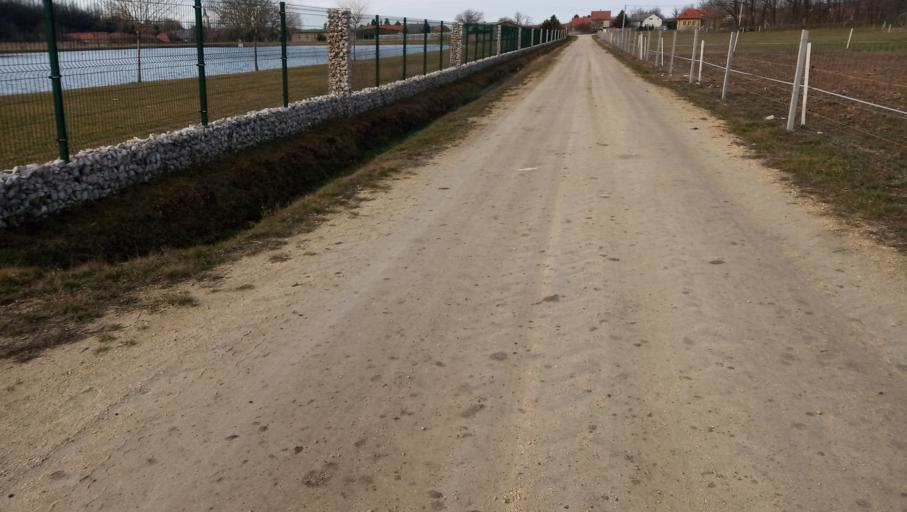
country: HU
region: Komarom-Esztergom
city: Piliscsev
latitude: 47.6806
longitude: 18.8269
